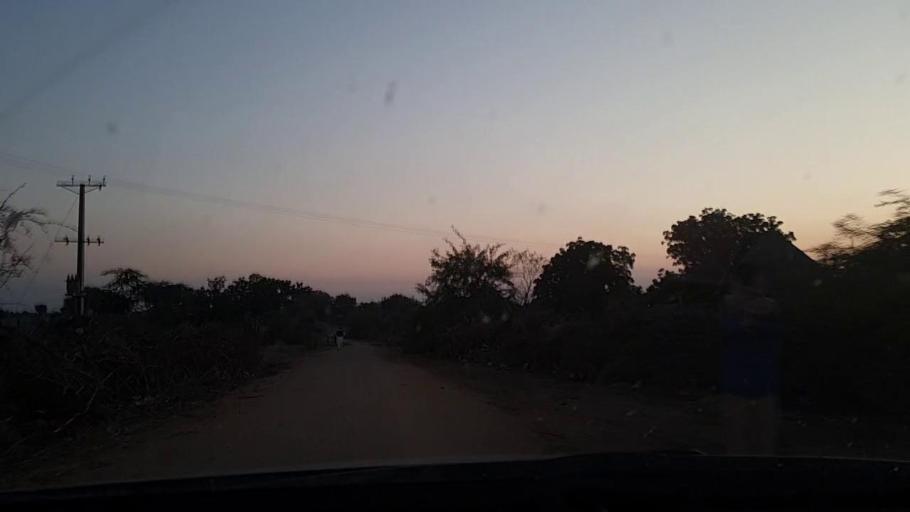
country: PK
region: Sindh
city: Tando Mittha Khan
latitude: 25.9233
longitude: 69.3287
